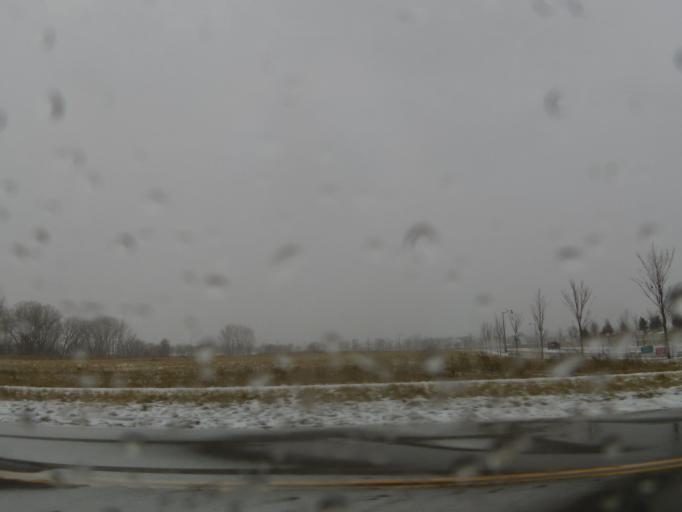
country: US
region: Minnesota
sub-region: Washington County
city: Oakdale
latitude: 44.9576
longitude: -92.9296
